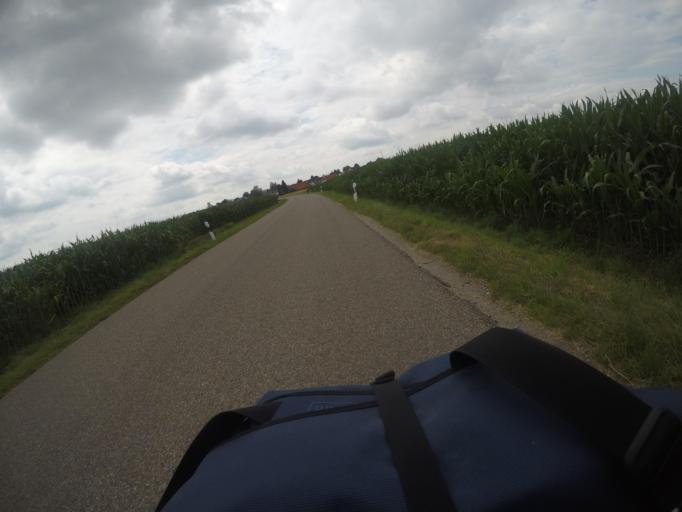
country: DE
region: Bavaria
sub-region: Swabia
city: Heimertingen
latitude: 48.0170
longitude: 10.1713
